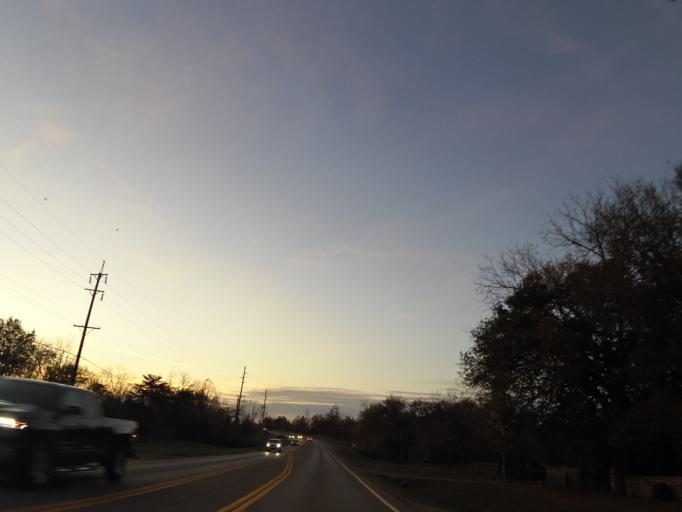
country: US
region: Kentucky
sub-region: Fayette County
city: Lexington-Fayette
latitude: 38.0395
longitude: -84.4093
